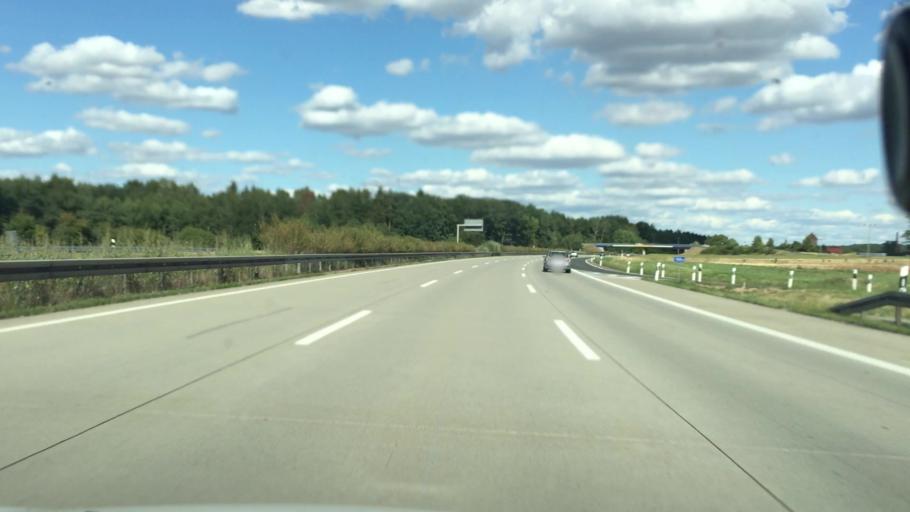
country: DE
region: Thuringia
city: Hermsdorf
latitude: 50.8914
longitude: 11.8790
